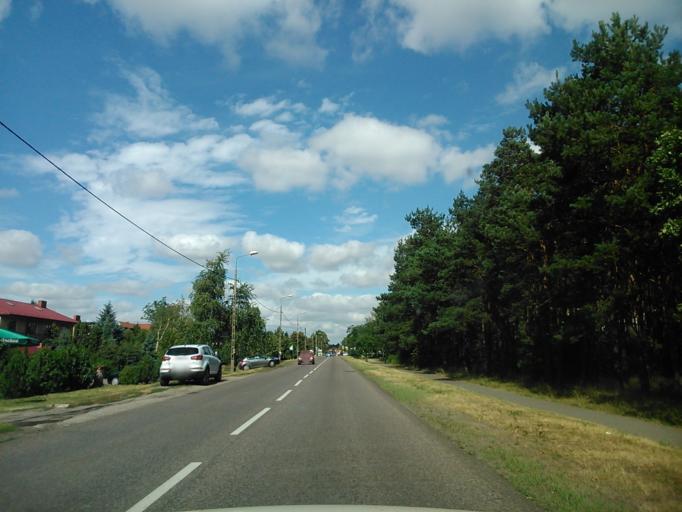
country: PL
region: Kujawsko-Pomorskie
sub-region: Powiat golubsko-dobrzynski
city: Golub-Dobrzyn
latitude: 53.1004
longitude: 19.0489
